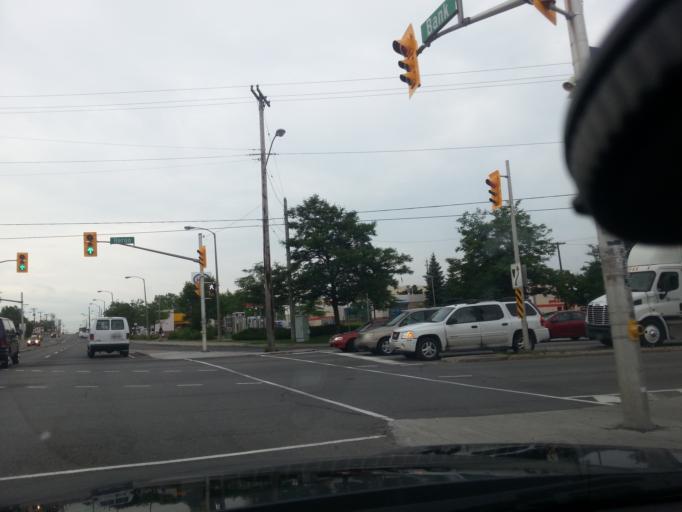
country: CA
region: Ontario
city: Ottawa
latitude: 45.3787
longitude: -75.6678
